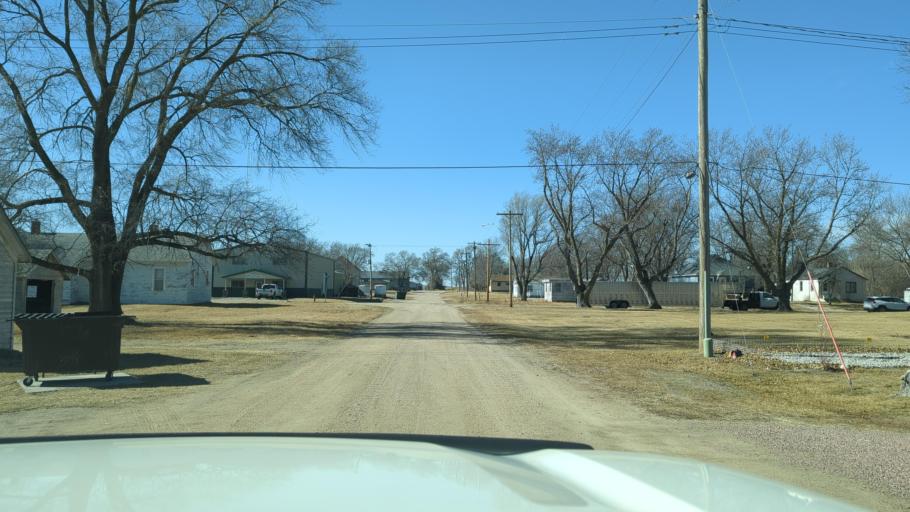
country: US
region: Nebraska
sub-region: Antelope County
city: Neligh
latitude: 42.2615
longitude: -98.3455
